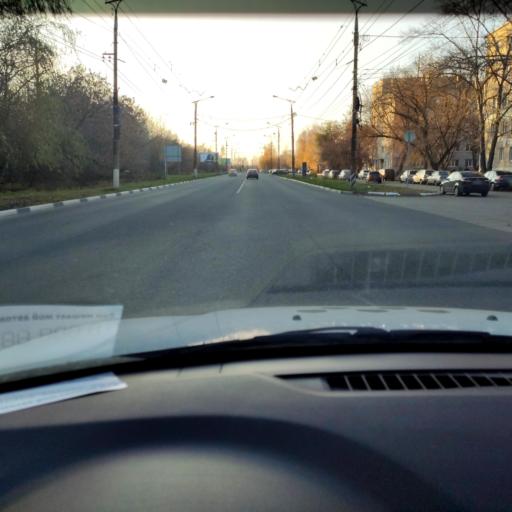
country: RU
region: Samara
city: Tol'yatti
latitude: 53.4984
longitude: 49.3964
